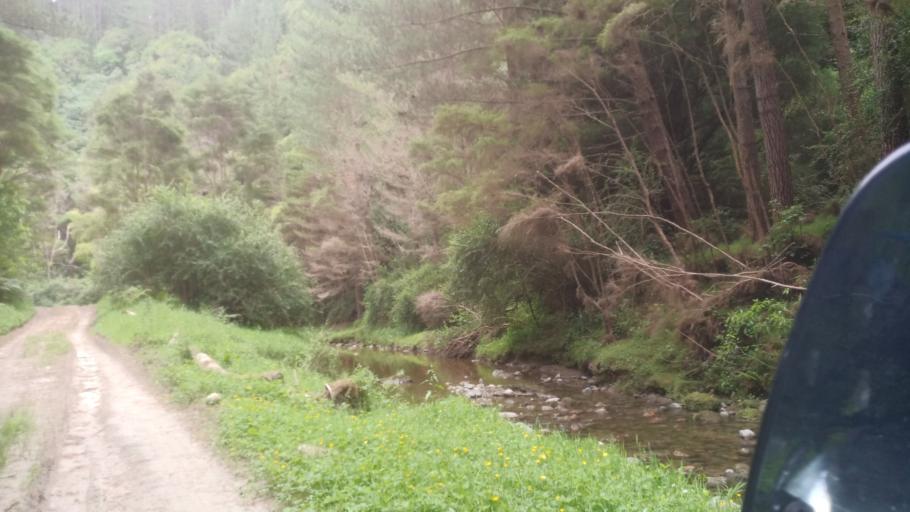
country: NZ
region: Gisborne
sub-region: Gisborne District
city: Gisborne
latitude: -38.4566
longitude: 177.9262
